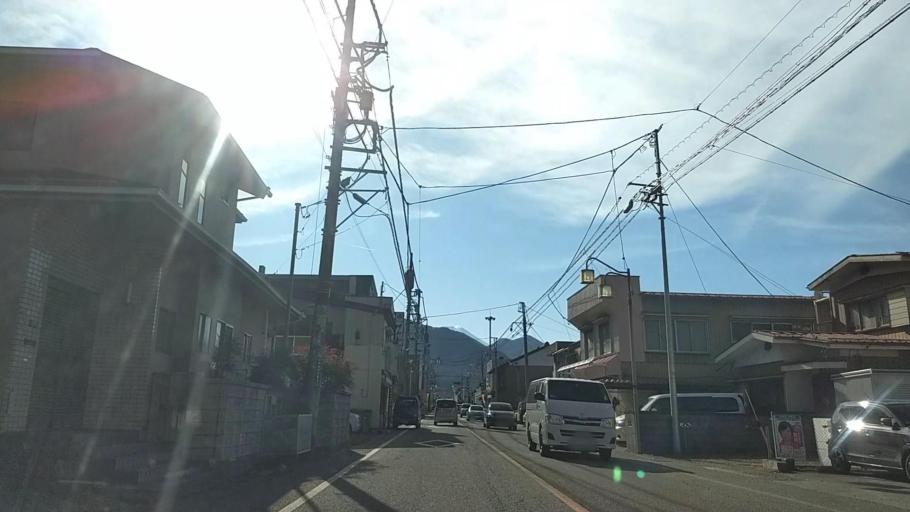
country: JP
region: Yamanashi
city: Otsuki
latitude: 35.5545
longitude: 138.9109
